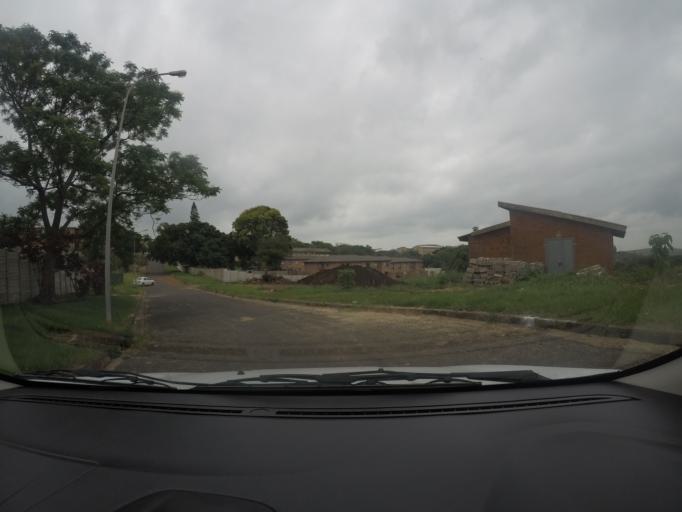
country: ZA
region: KwaZulu-Natal
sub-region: uThungulu District Municipality
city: Empangeni
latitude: -28.7437
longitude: 31.8954
